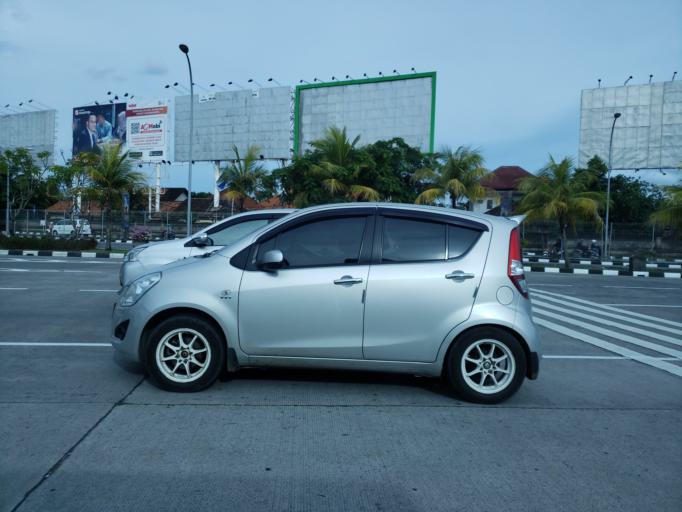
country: ID
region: Bali
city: Kelanabian
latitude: -8.7423
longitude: 115.1675
